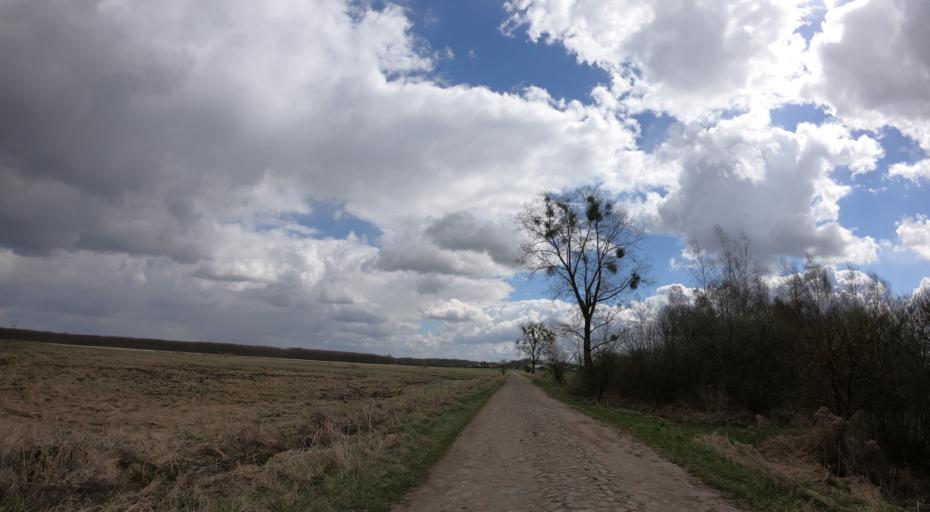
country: PL
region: West Pomeranian Voivodeship
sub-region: Powiat drawski
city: Drawsko Pomorskie
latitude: 53.5463
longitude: 15.8620
